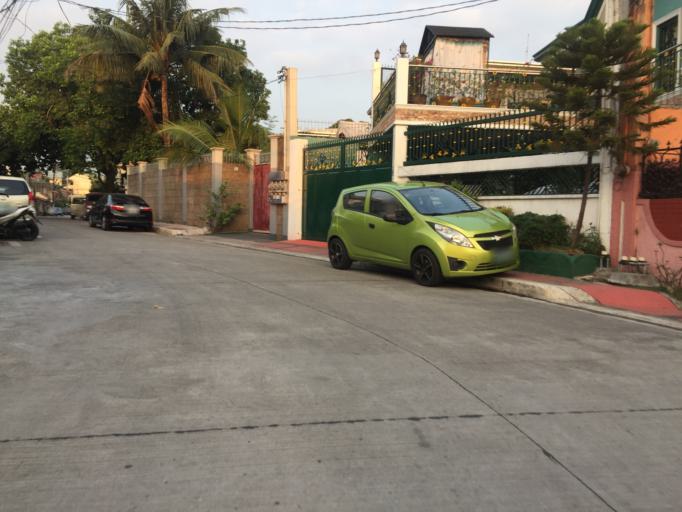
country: PH
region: Calabarzon
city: Bagong Pagasa
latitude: 14.6777
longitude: 121.0237
